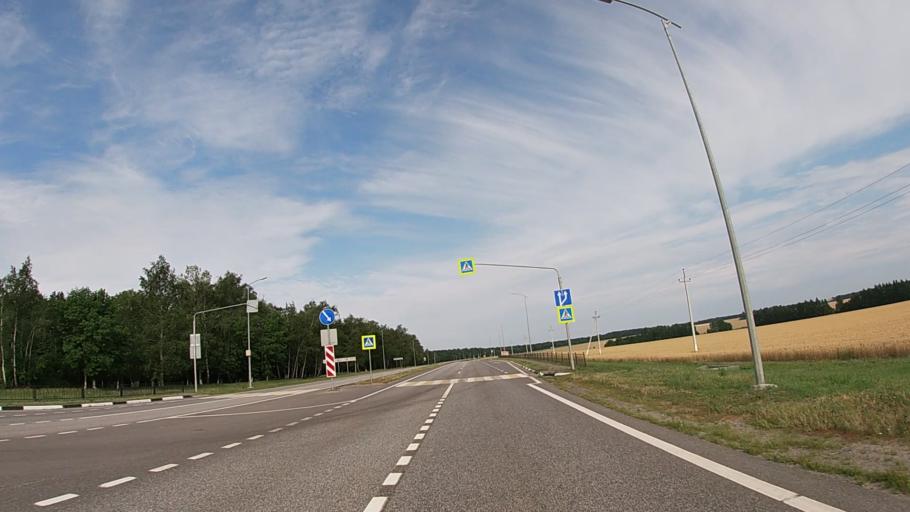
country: RU
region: Belgorod
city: Borisovka
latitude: 50.7505
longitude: 35.9834
